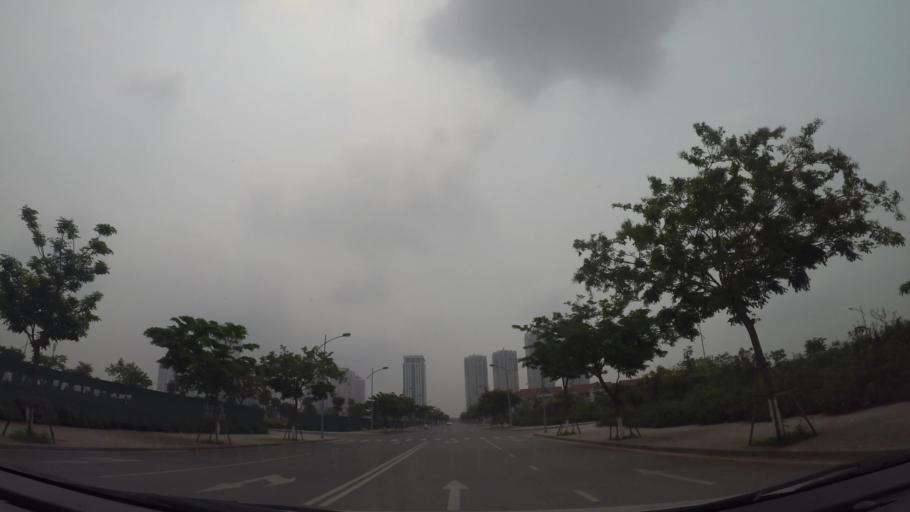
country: VN
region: Ha Noi
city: Ha Dong
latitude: 20.9787
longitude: 105.7539
